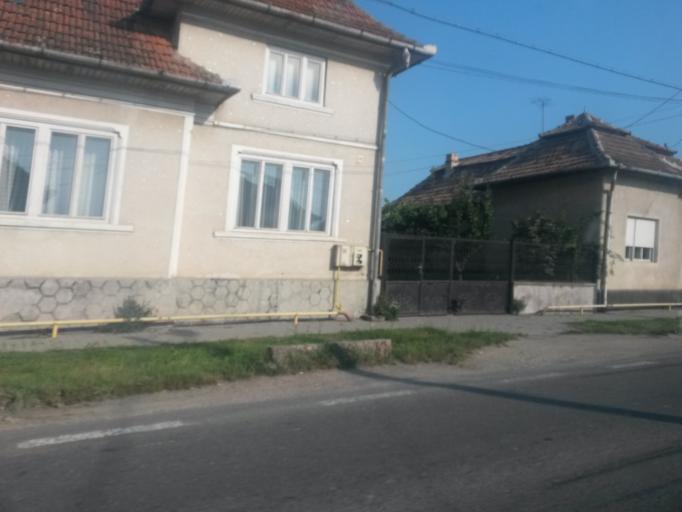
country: RO
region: Alba
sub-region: Comuna Unirea
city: Unirea
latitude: 46.3991
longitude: 23.8092
